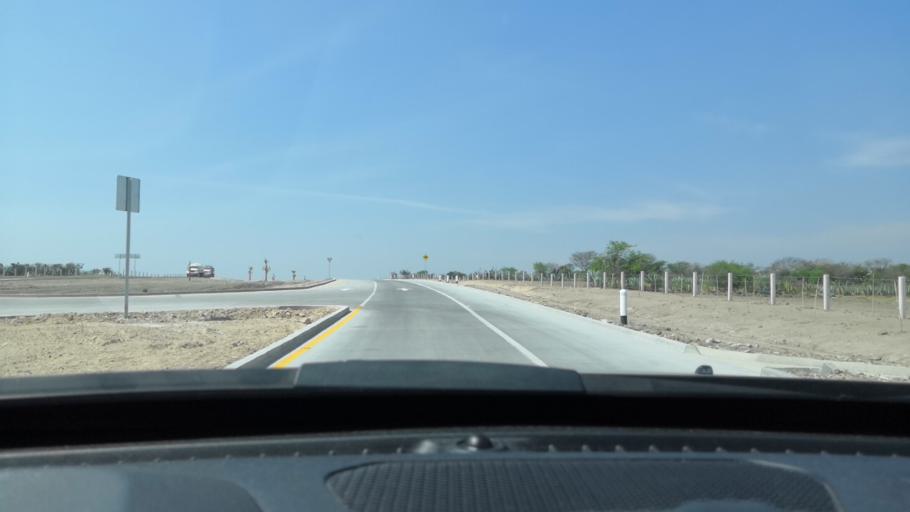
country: MX
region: Guanajuato
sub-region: Leon
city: Centro Familiar la Soledad
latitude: 21.0943
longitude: -101.7889
